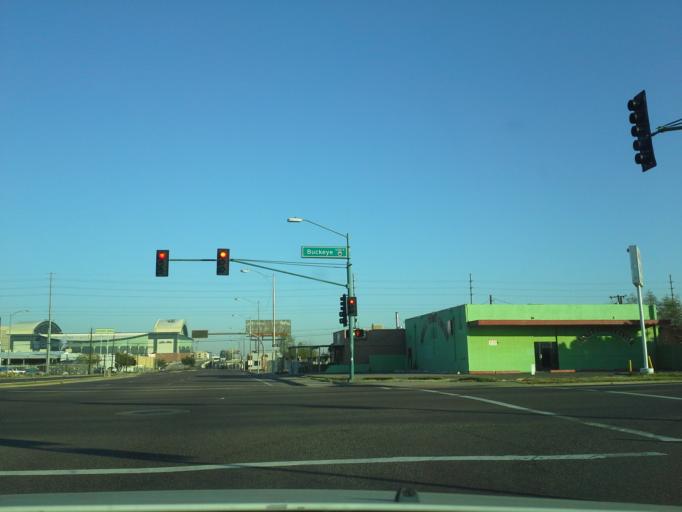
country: US
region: Arizona
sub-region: Maricopa County
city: Phoenix
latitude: 33.4366
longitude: -112.0650
